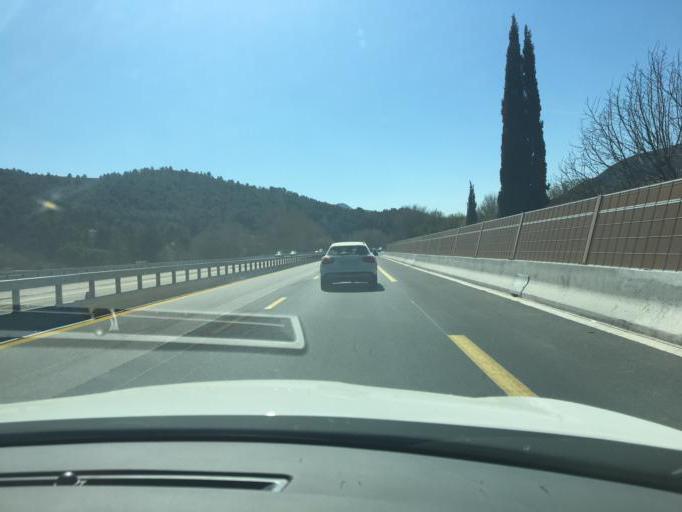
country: FR
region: Provence-Alpes-Cote d'Azur
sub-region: Departement des Bouches-du-Rhone
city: La Destrousse
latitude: 43.3782
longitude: 5.6075
